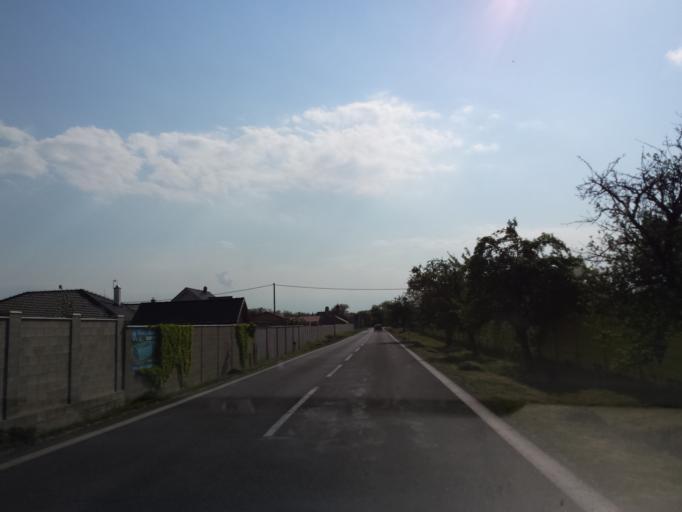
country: SK
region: Bratislavsky
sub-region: Okres Malacky
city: Malacky
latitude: 48.4143
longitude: 16.9370
